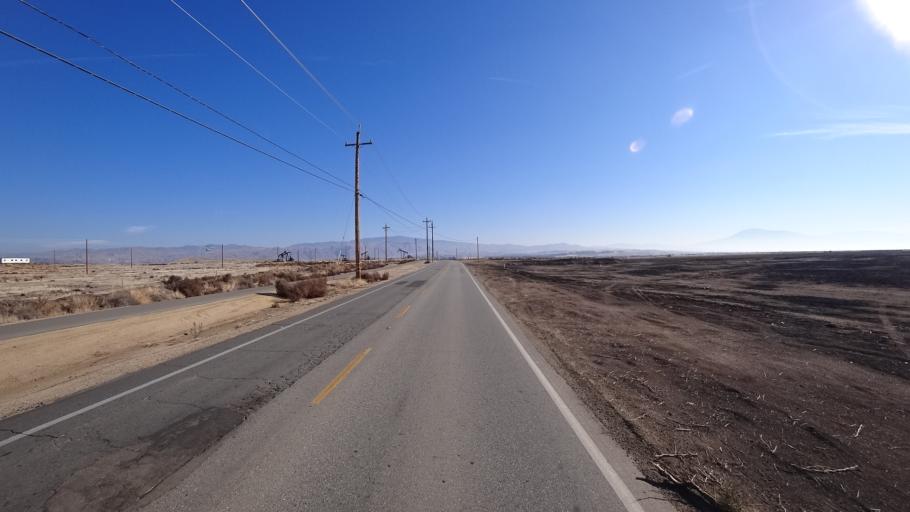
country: US
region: California
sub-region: Kern County
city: Oildale
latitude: 35.4125
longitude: -118.9087
